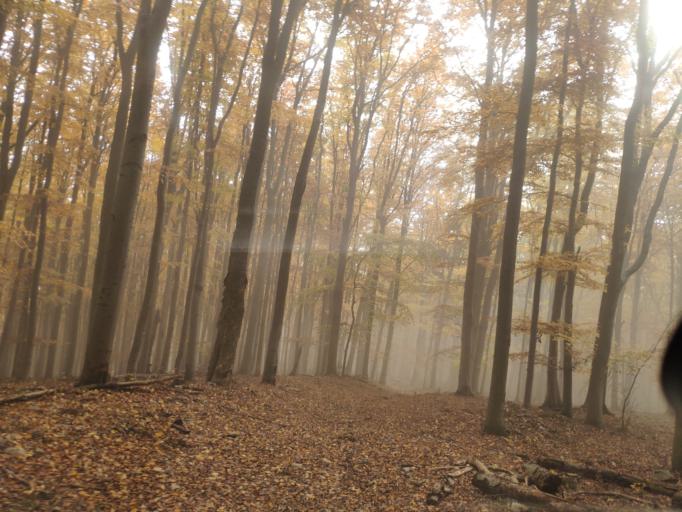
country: SK
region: Kosicky
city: Moldava nad Bodvou
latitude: 48.7305
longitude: 21.0144
